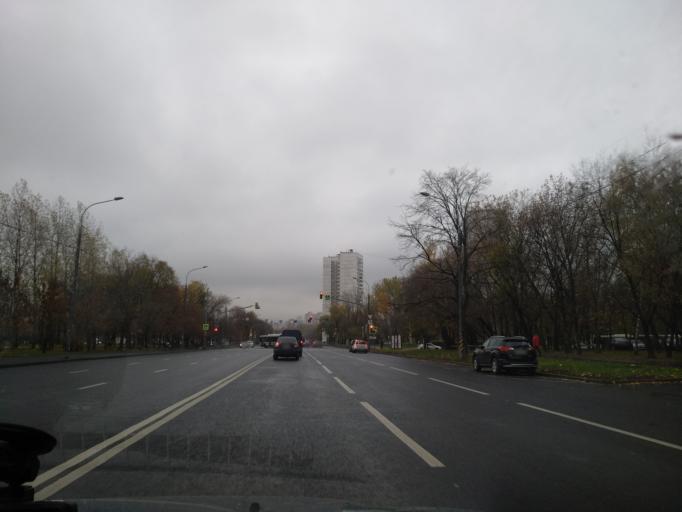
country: RU
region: Moscow
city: Kozeyevo
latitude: 55.8701
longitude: 37.6199
